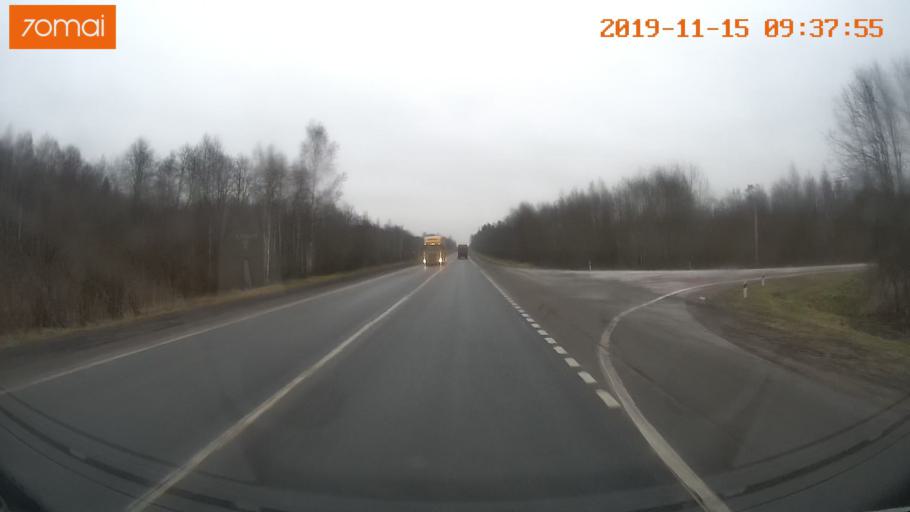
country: RU
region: Vologda
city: Sheksna
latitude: 59.2366
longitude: 38.4457
